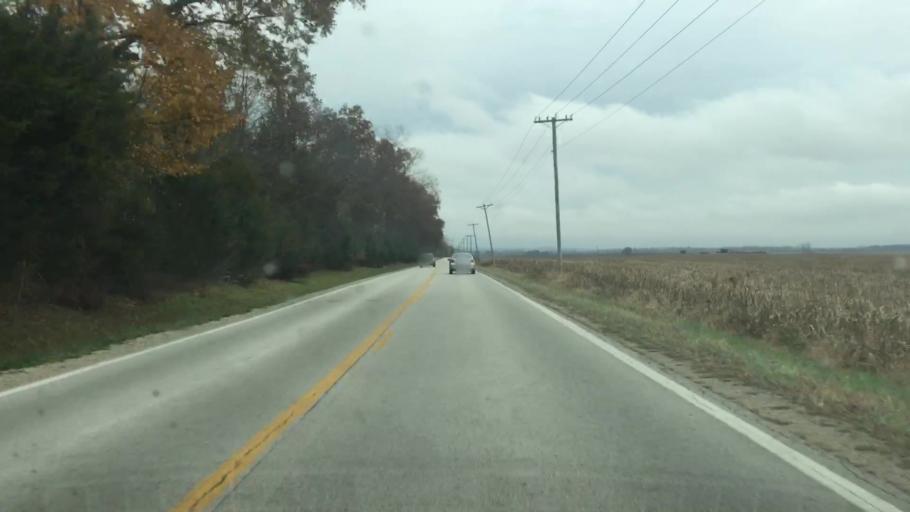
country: US
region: Missouri
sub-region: Gasconade County
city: Hermann
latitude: 38.7223
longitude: -91.4994
